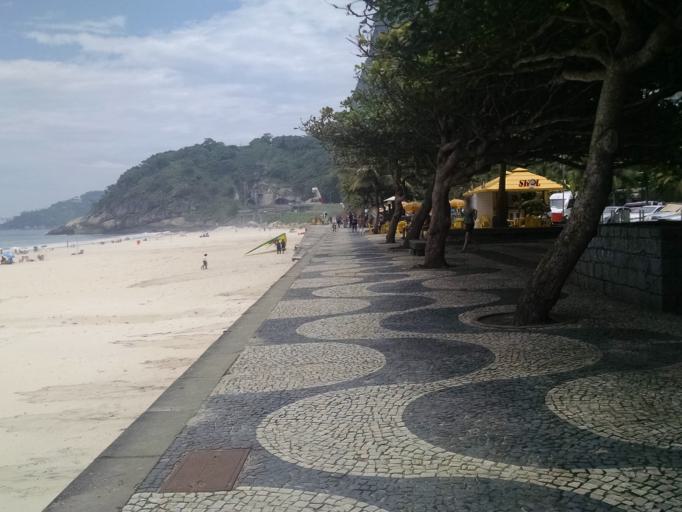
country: BR
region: Rio de Janeiro
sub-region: Rio De Janeiro
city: Rio de Janeiro
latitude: -23.0005
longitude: -43.2707
